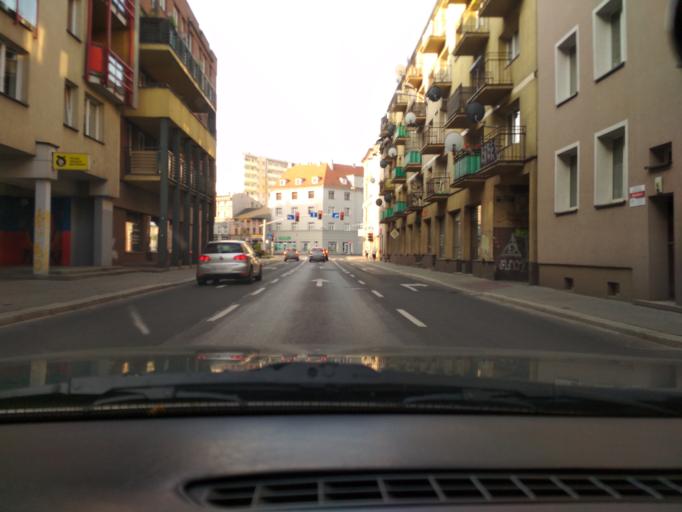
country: PL
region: Silesian Voivodeship
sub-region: Gliwice
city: Gliwice
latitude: 50.2907
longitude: 18.6680
